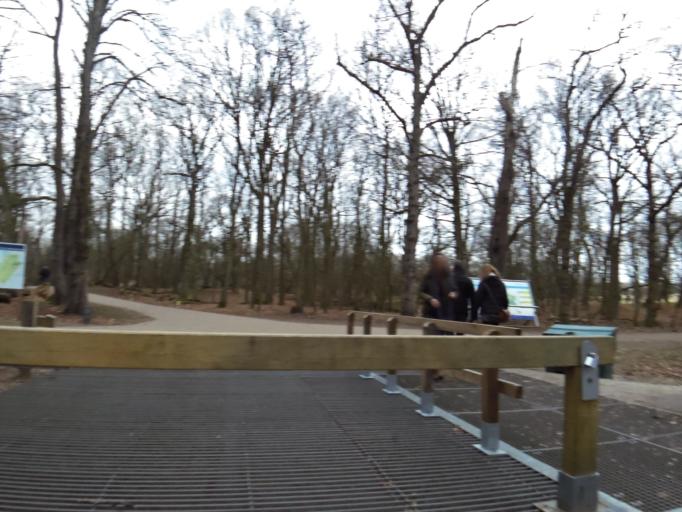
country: NL
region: North Holland
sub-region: Gemeente Bloemendaal
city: Bennebroek
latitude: 52.3315
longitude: 4.5648
